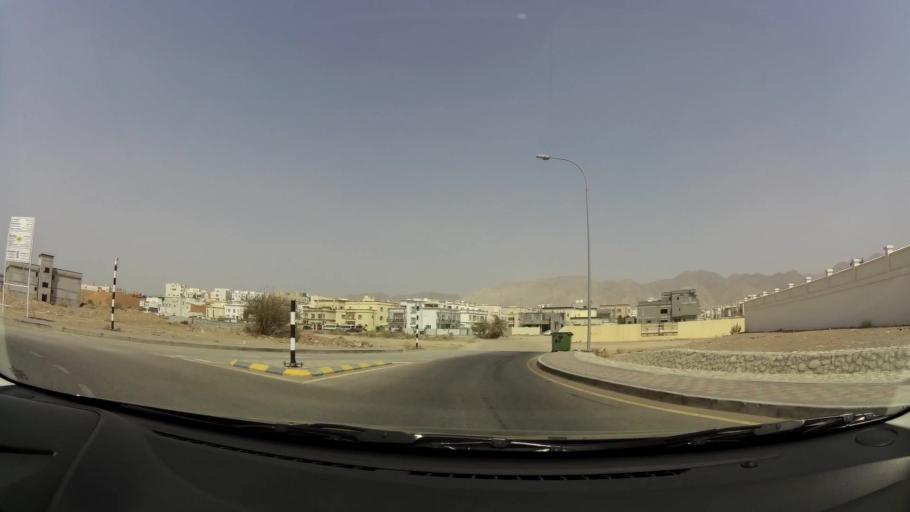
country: OM
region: Muhafazat Masqat
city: Bawshar
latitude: 23.5693
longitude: 58.3840
